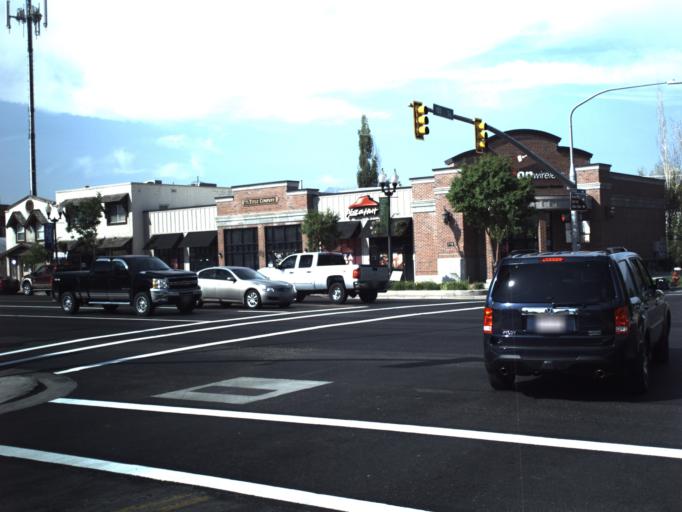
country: US
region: Utah
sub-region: Wasatch County
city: Heber
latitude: 40.5064
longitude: -111.4132
